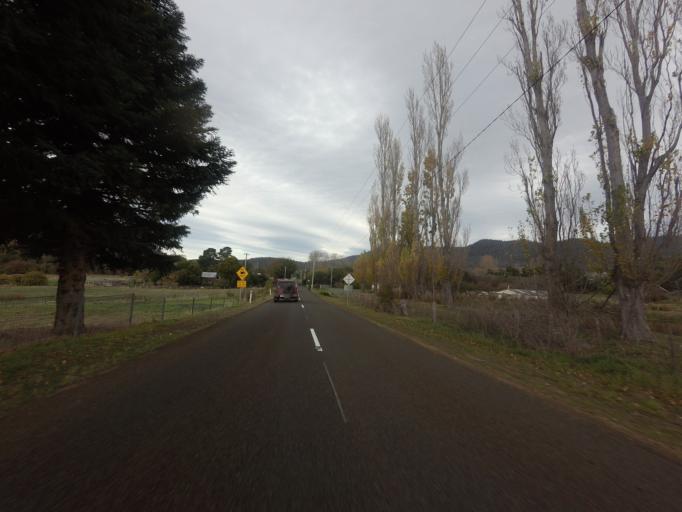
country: AU
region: Tasmania
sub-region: Brighton
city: Bridgewater
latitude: -42.6567
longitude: 147.1261
